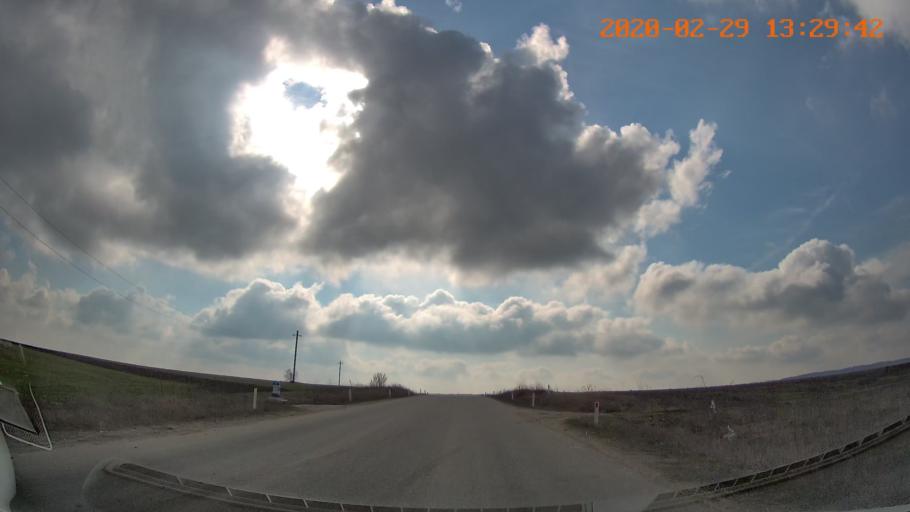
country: MD
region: Telenesti
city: Camenca
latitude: 47.8944
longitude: 28.6345
